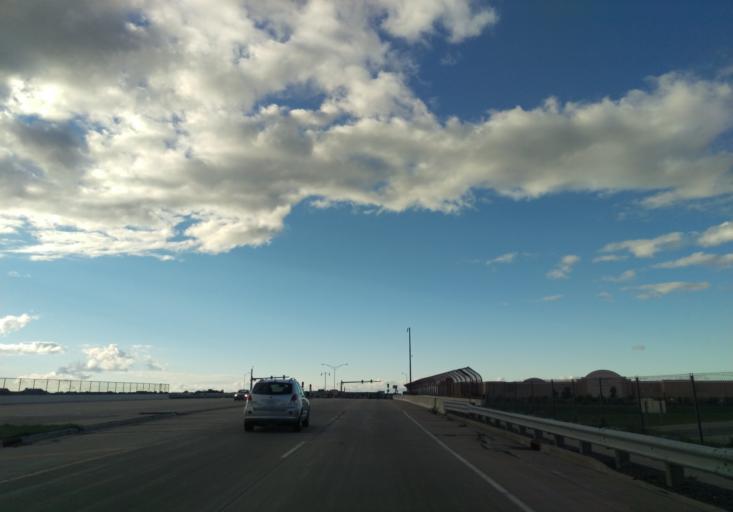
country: US
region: Wisconsin
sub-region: Dane County
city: Sun Prairie
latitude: 43.1609
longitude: -89.2669
